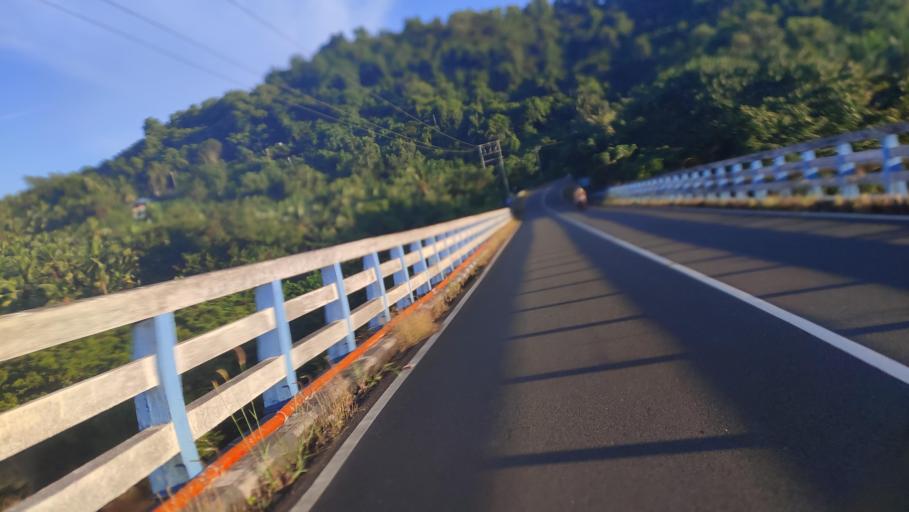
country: IN
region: Kerala
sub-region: Kasaragod District
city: Kasaragod
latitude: 12.4621
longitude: 75.0890
